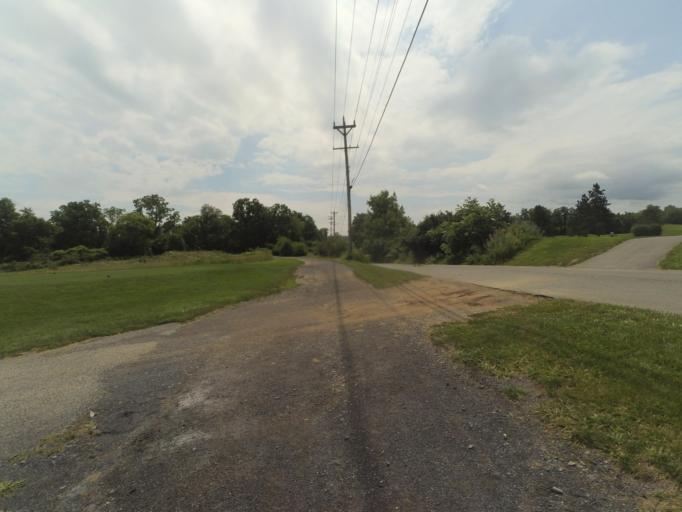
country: US
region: Pennsylvania
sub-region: Centre County
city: State College
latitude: 40.7867
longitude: -77.8770
